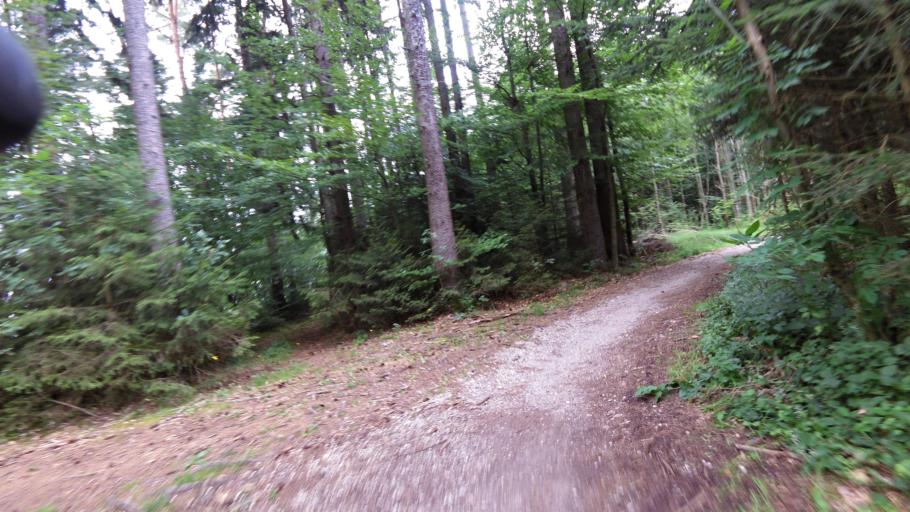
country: DE
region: Bavaria
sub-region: Upper Bavaria
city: Chieming
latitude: 47.8678
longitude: 12.5206
